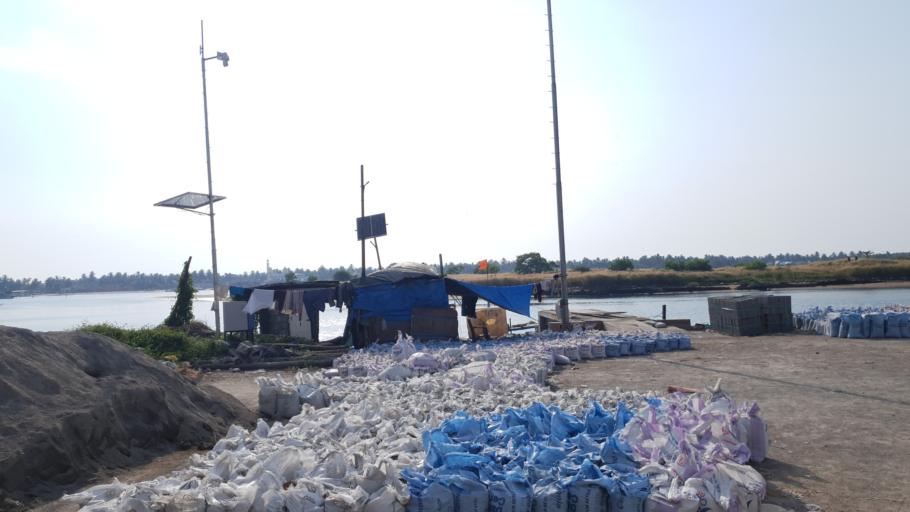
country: IN
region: Karnataka
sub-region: Dakshina Kannada
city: Mangalore
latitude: 12.8642
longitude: 74.8312
